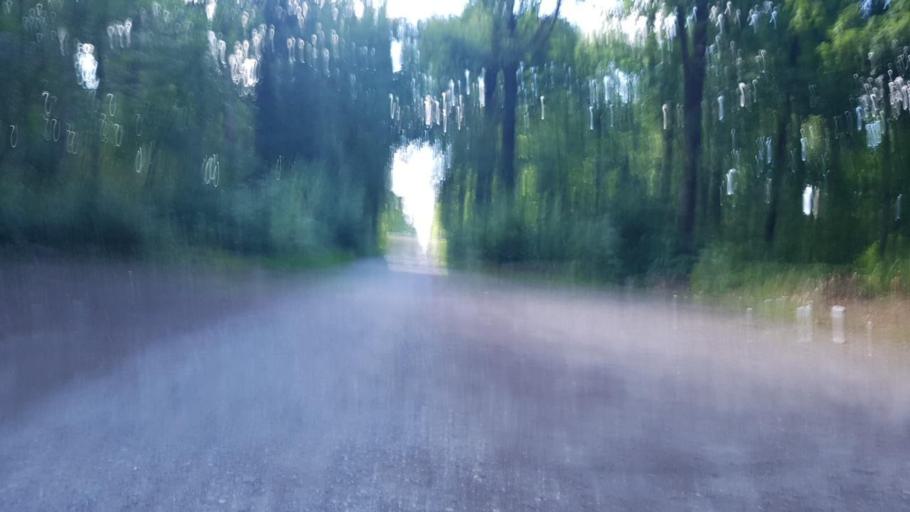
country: FR
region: Picardie
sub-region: Departement de l'Oise
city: Ver-sur-Launette
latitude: 49.1415
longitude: 2.6537
